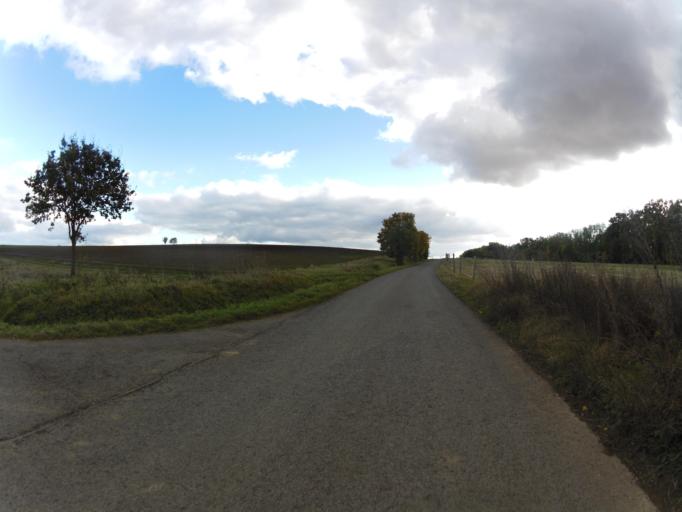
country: DE
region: Bavaria
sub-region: Regierungsbezirk Unterfranken
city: Kurnach
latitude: 49.8641
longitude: 10.0062
